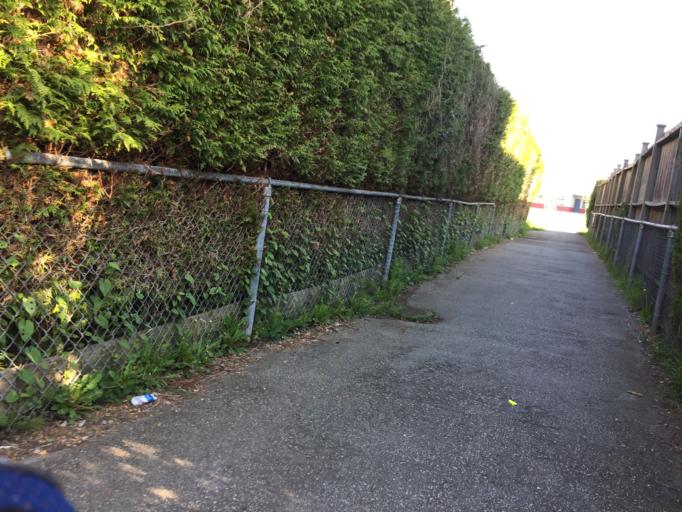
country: CA
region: British Columbia
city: Richmond
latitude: 49.1528
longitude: -123.1442
